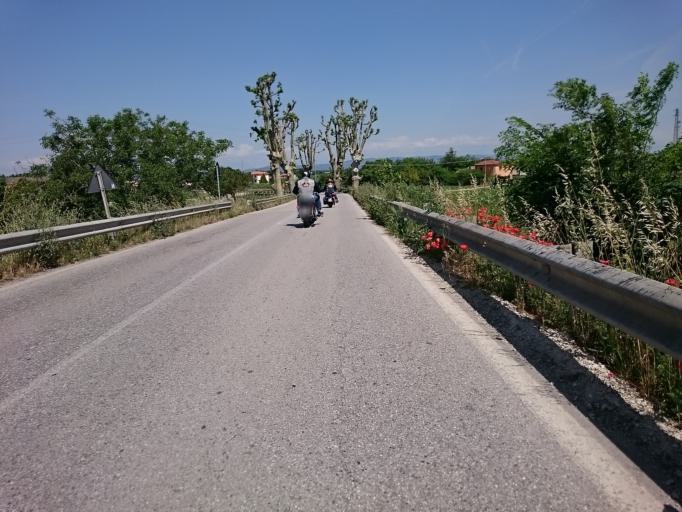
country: IT
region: Veneto
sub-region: Provincia di Vicenza
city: Noventa Vicentina
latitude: 45.2619
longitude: 11.5663
